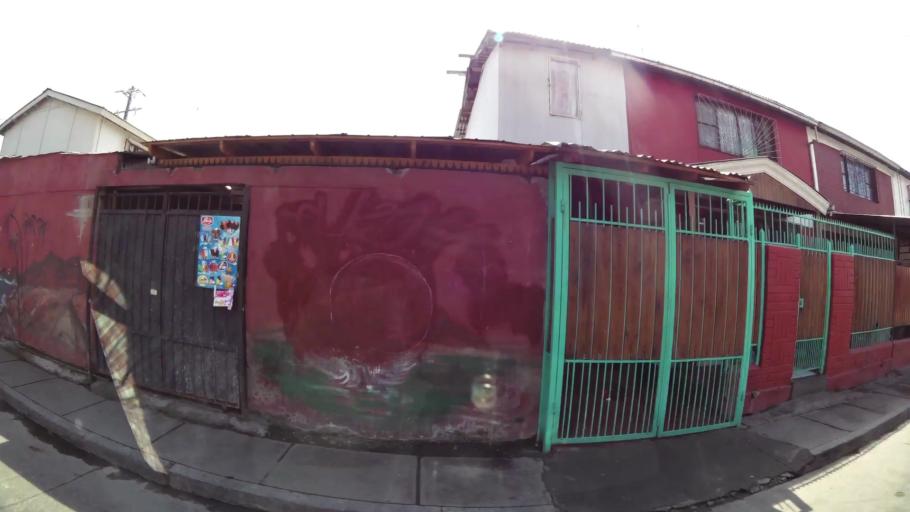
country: CL
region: Santiago Metropolitan
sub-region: Provincia de Santiago
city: La Pintana
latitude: -33.5912
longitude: -70.6041
